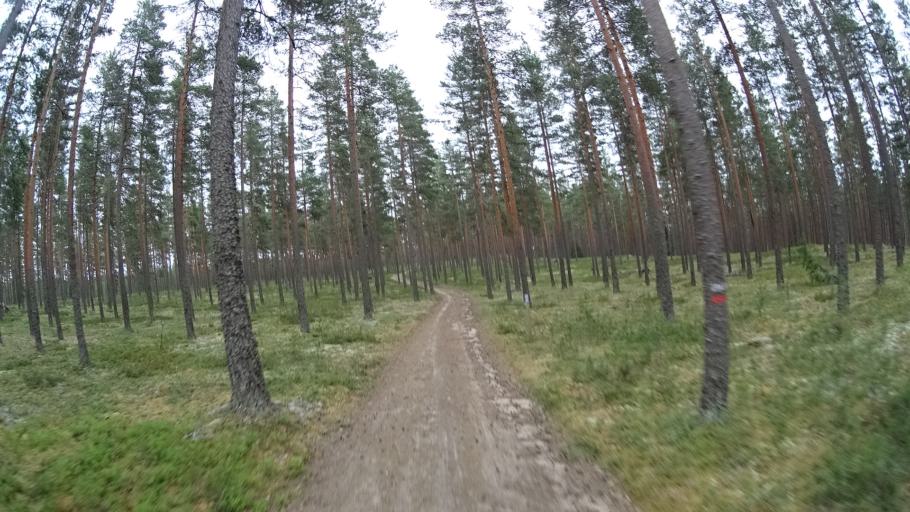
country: FI
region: Satakunta
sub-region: Pohjois-Satakunta
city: Jaemijaervi
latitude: 61.7641
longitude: 22.7681
